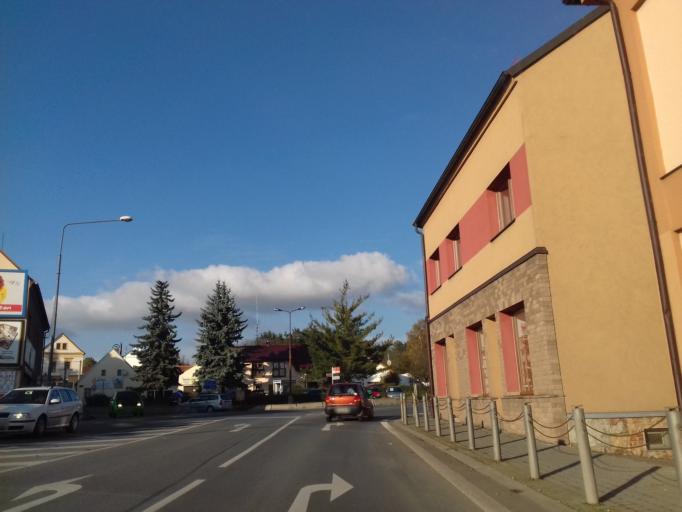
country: CZ
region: Plzensky
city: Stod
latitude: 49.6402
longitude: 13.1644
